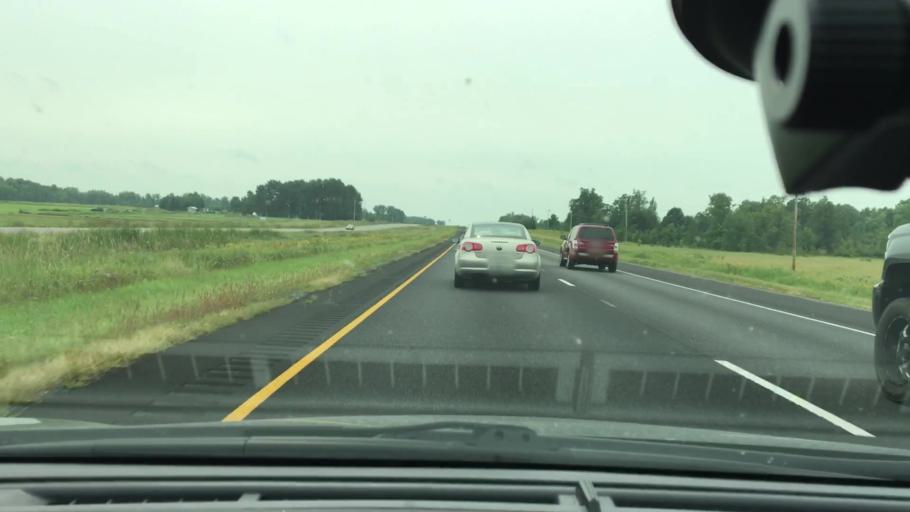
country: US
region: Minnesota
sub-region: Mille Lacs County
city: Milaca
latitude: 45.9013
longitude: -93.6622
